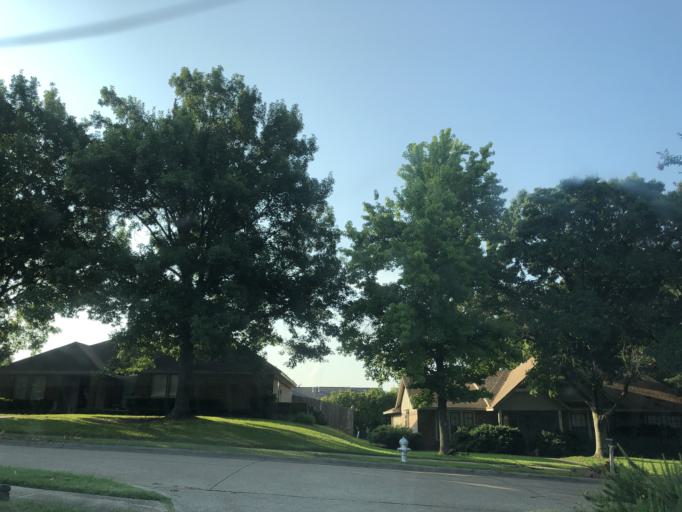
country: US
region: Texas
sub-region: Dallas County
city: Garland
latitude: 32.8652
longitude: -96.6226
